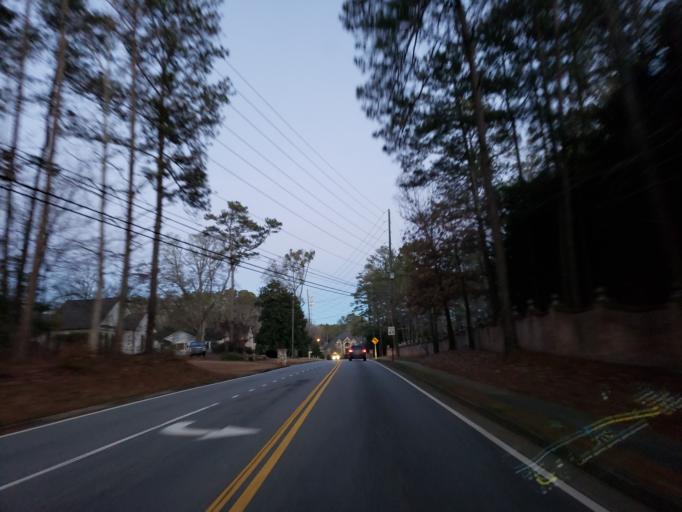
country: US
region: Georgia
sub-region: Cobb County
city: Kennesaw
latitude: 33.9652
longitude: -84.6739
